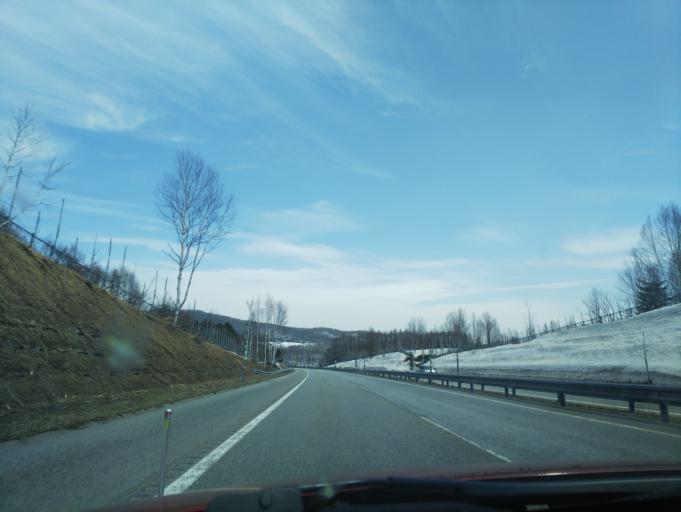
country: JP
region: Hokkaido
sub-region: Asahikawa-shi
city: Asahikawa
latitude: 43.7923
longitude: 142.2735
